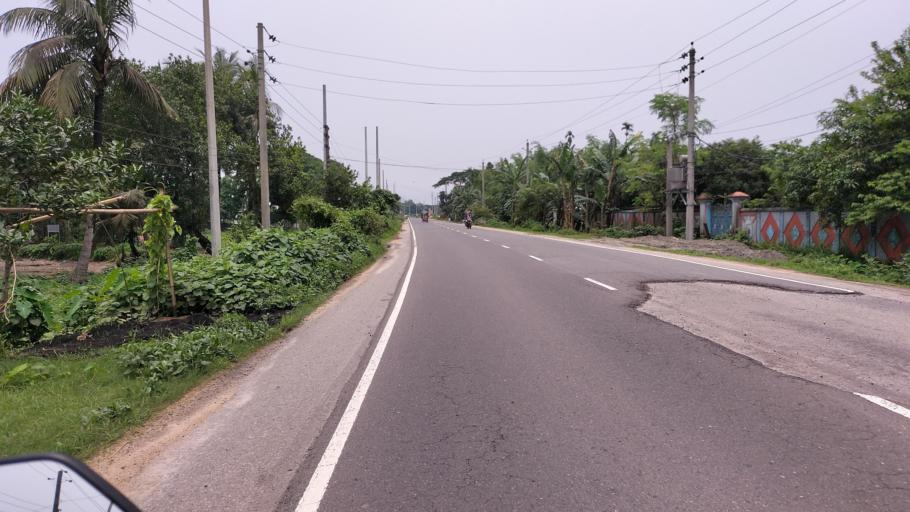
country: BD
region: Dhaka
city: Mymensingh
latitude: 24.7796
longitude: 90.4742
